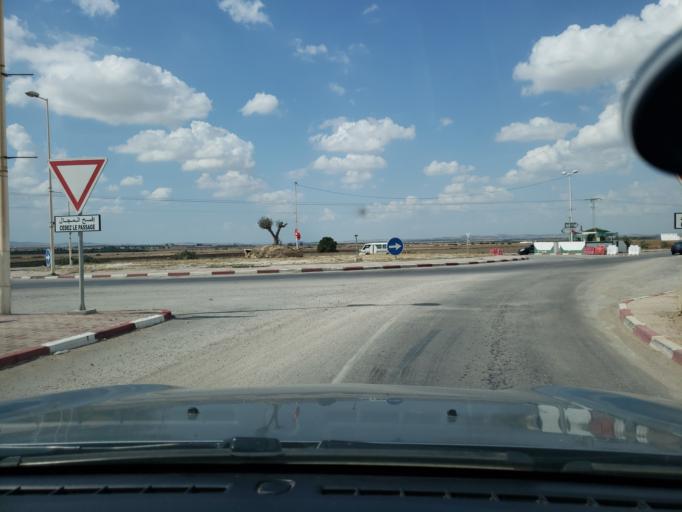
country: TN
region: Tunis
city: La Mohammedia
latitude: 36.5643
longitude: 10.0825
